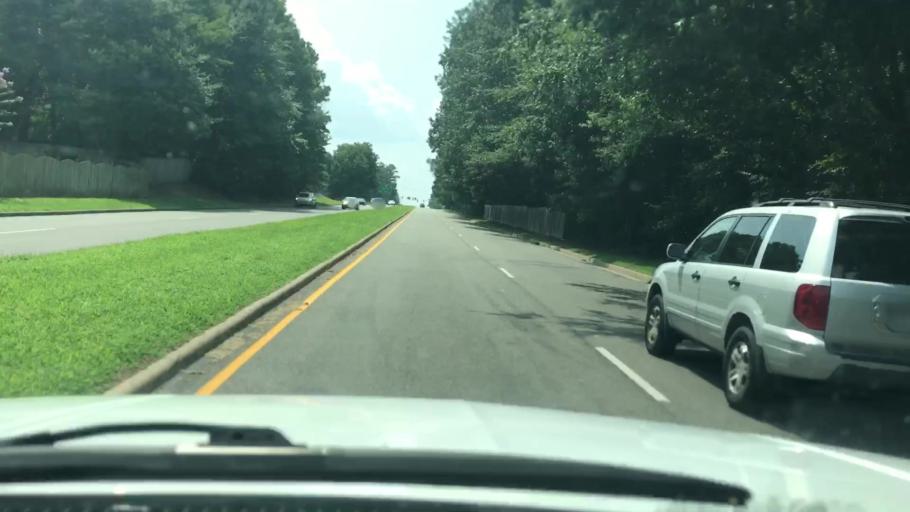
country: US
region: Virginia
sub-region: Henrico County
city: Short Pump
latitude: 37.6247
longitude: -77.6016
